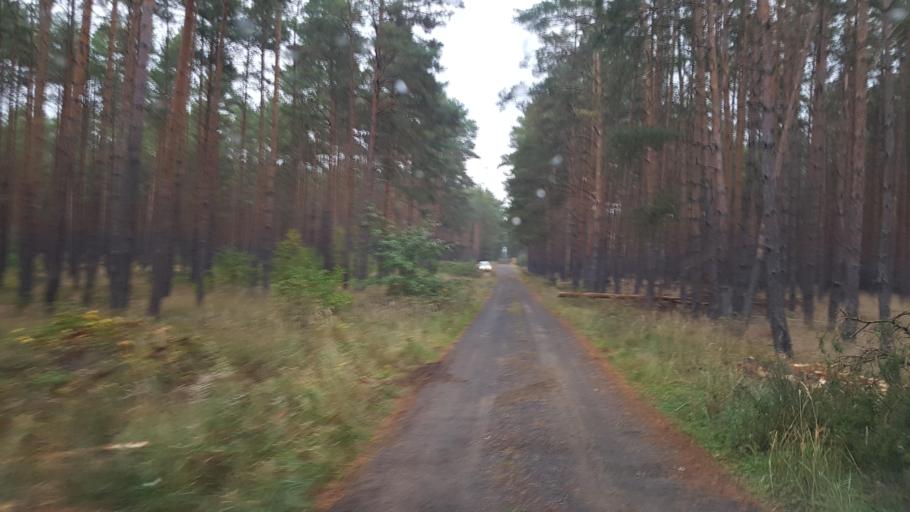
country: DE
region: Brandenburg
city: Schlieben
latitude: 51.7455
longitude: 13.3942
